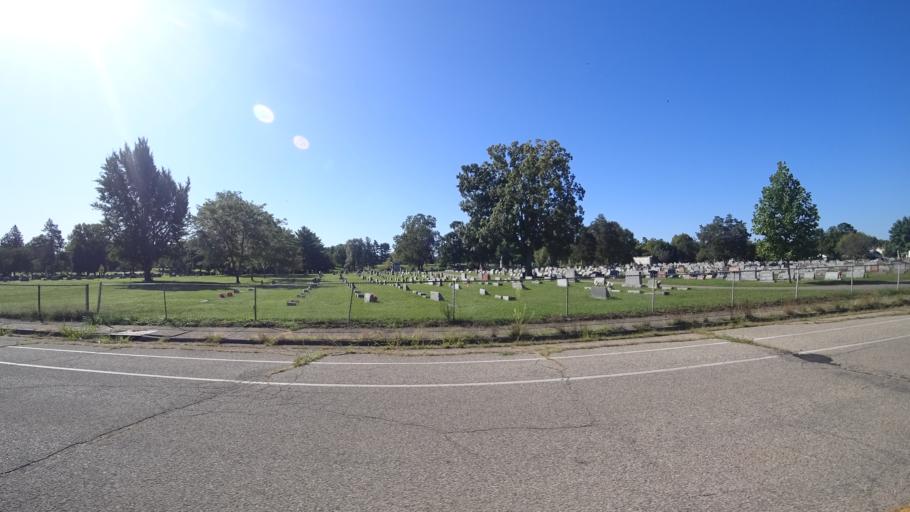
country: US
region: Ohio
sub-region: Butler County
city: Hamilton
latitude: 39.4082
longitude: -84.5423
